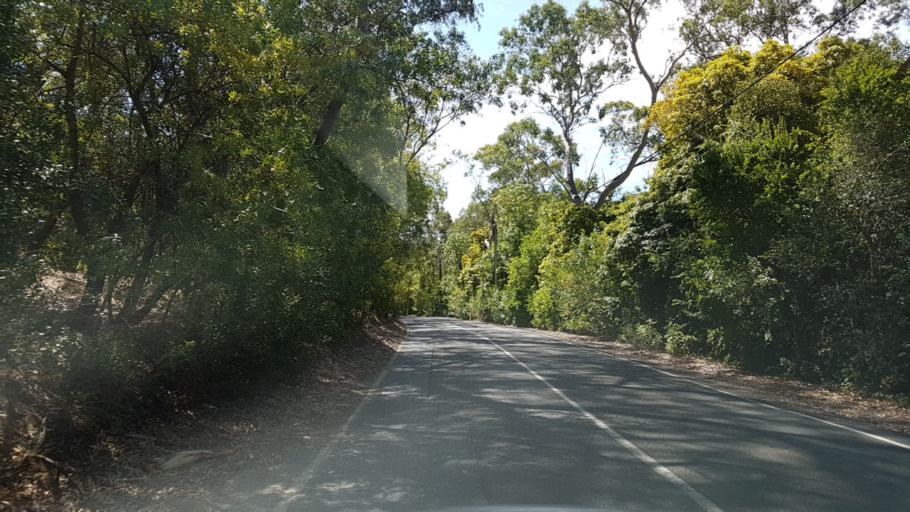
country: AU
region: South Australia
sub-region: Mitcham
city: Belair
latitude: -35.0033
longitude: 138.6328
